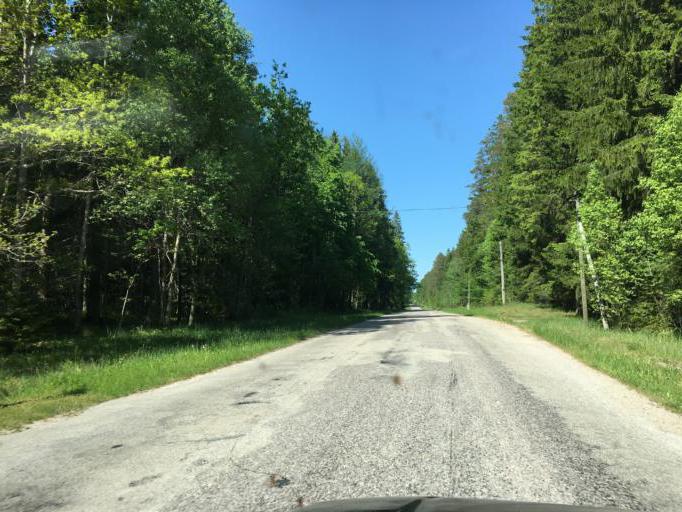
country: LV
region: Dundaga
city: Dundaga
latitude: 57.4841
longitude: 22.3400
